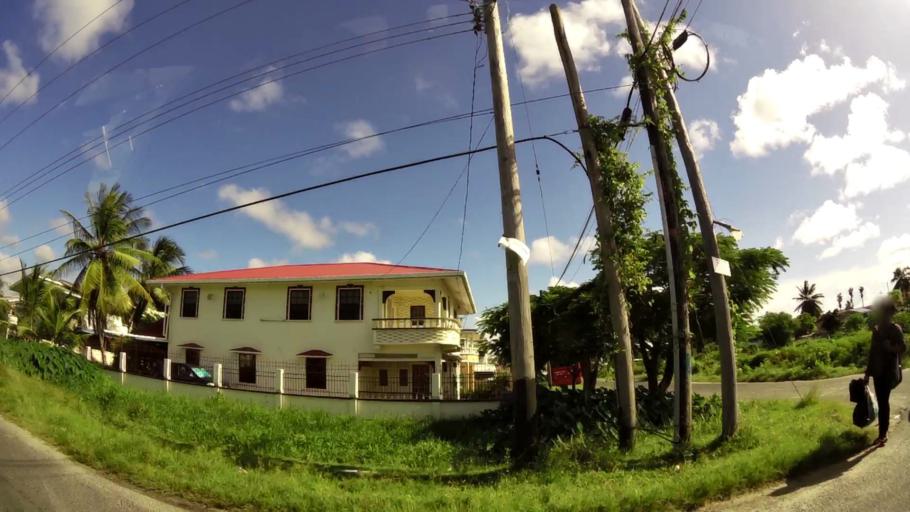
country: GY
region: Demerara-Mahaica
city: Georgetown
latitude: 6.8147
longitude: -58.1322
